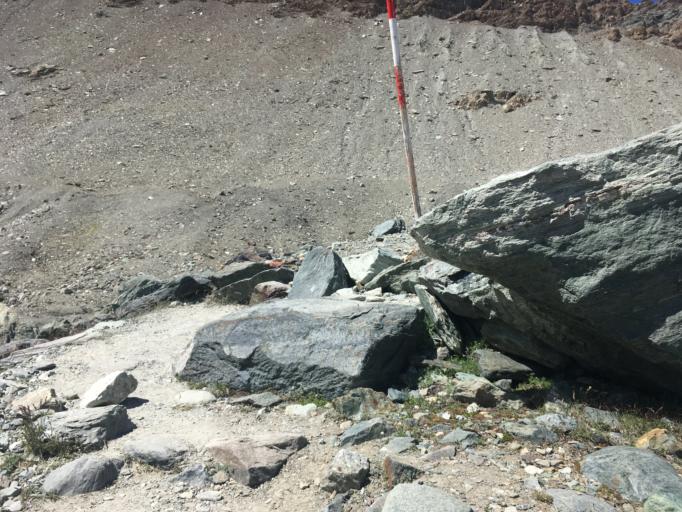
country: CH
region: Valais
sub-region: Visp District
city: Zermatt
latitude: 45.9849
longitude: 7.6932
